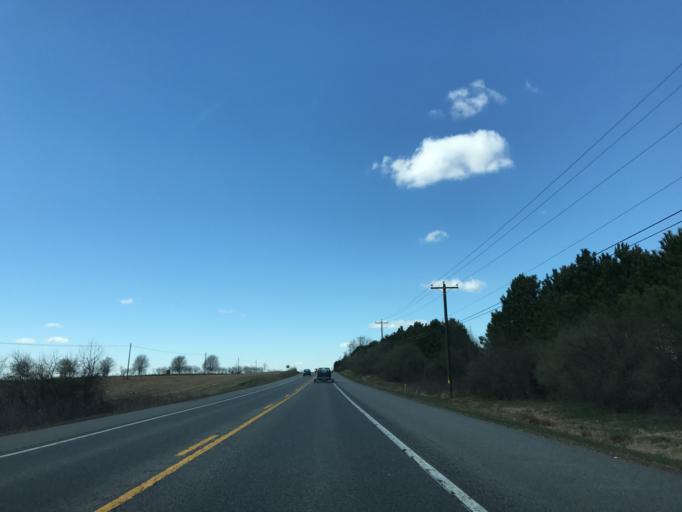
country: US
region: Maryland
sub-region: Queen Anne's County
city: Kingstown
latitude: 39.1854
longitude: -76.0121
